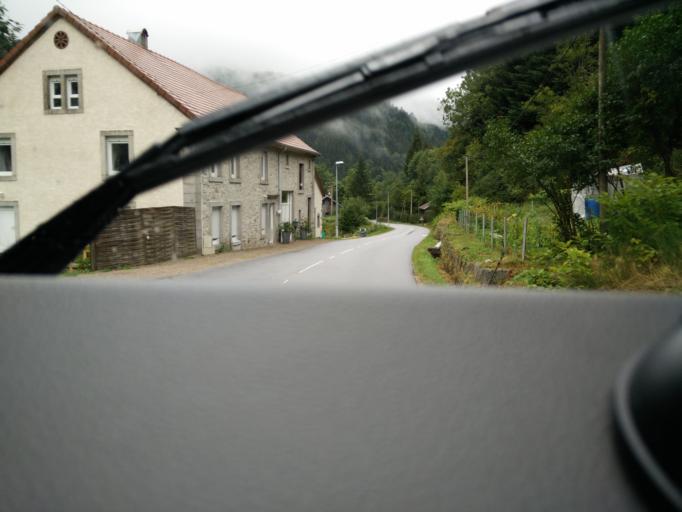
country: FR
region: Lorraine
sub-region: Departement des Vosges
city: Plainfaing
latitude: 48.1222
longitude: 7.0337
